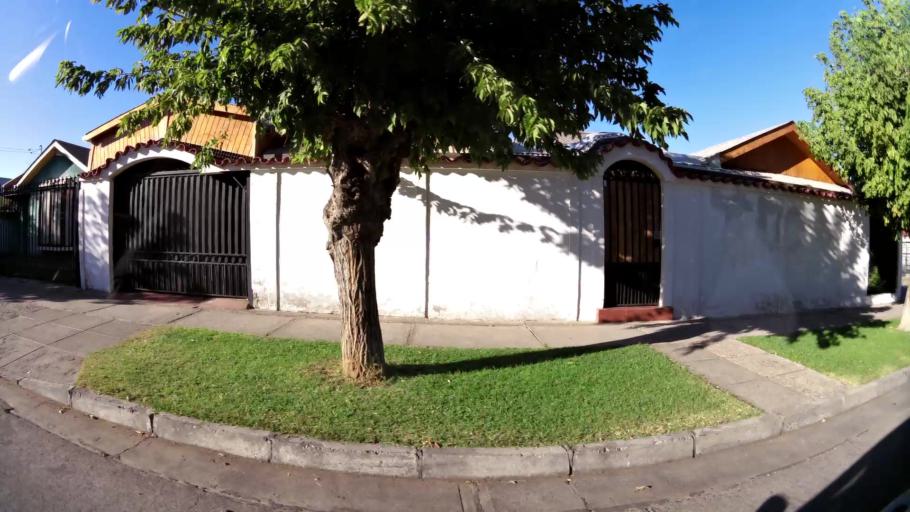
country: CL
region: O'Higgins
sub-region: Provincia de Cachapoal
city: Rancagua
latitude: -34.1710
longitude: -70.7184
